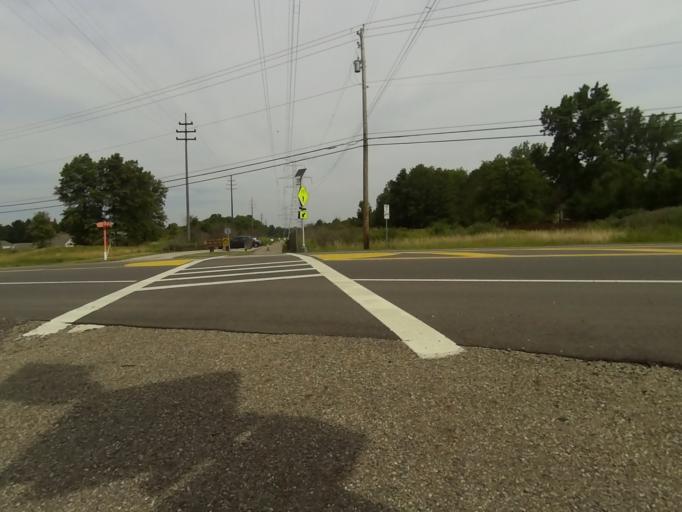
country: US
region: Ohio
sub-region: Summit County
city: Northfield
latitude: 41.3144
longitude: -81.5631
